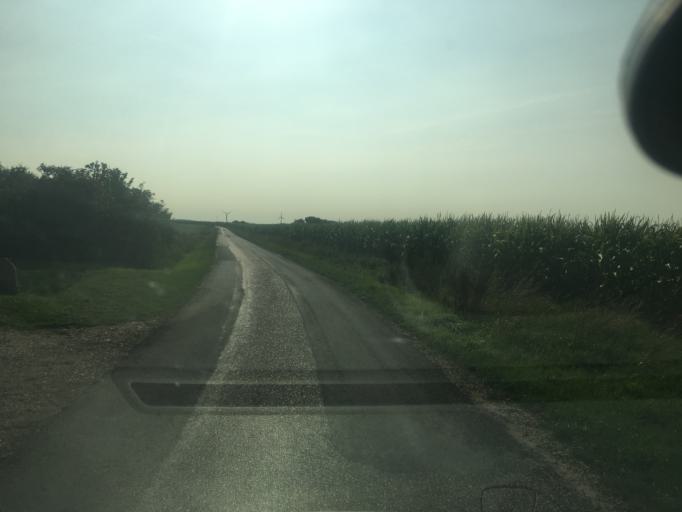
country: DK
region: South Denmark
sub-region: Tonder Kommune
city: Logumkloster
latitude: 54.9966
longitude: 8.9188
